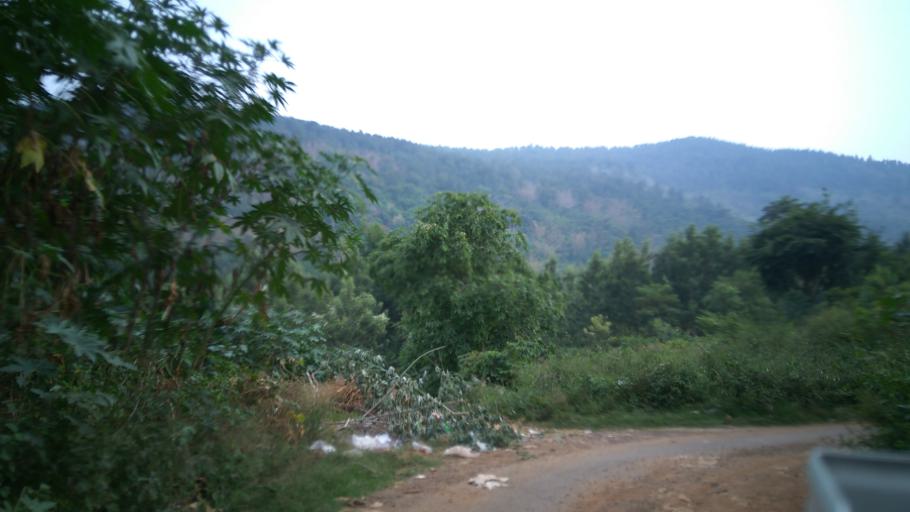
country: IN
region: Tamil Nadu
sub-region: Dharmapuri
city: Mallapuram
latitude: 11.8657
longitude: 78.1931
